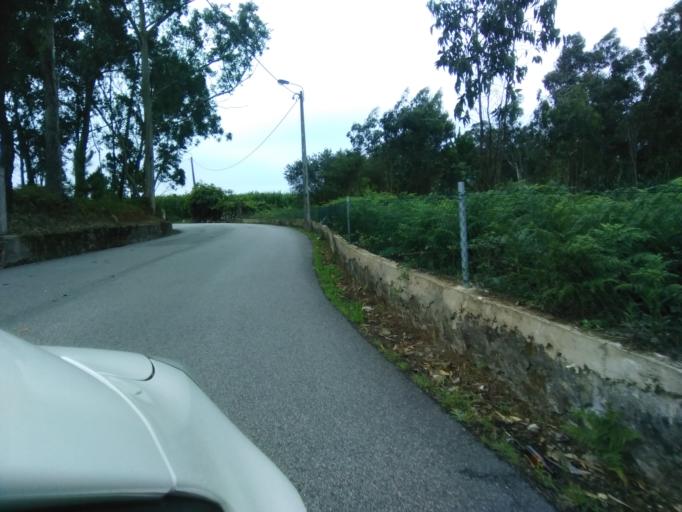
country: PT
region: Porto
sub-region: Matosinhos
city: Lavra
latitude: 41.2455
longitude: -8.7160
